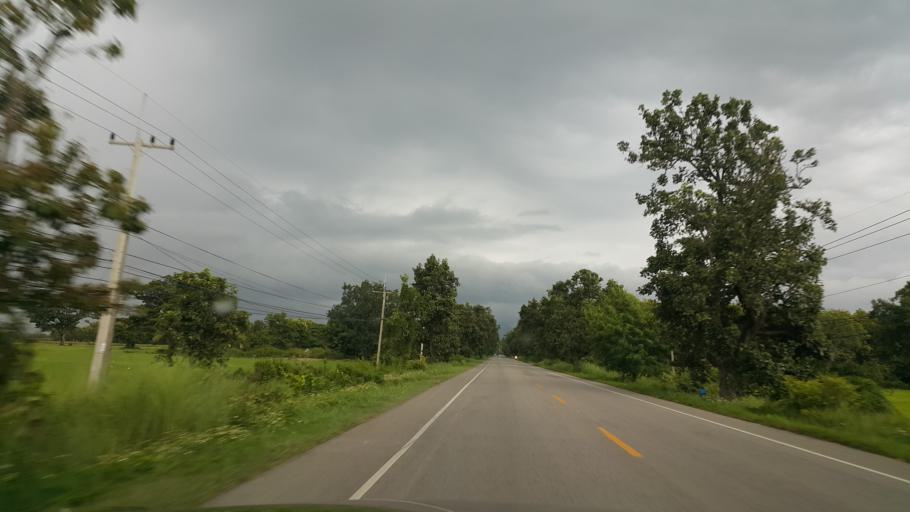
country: TH
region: Phayao
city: Dok Kham Tai
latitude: 19.2119
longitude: 100.0381
